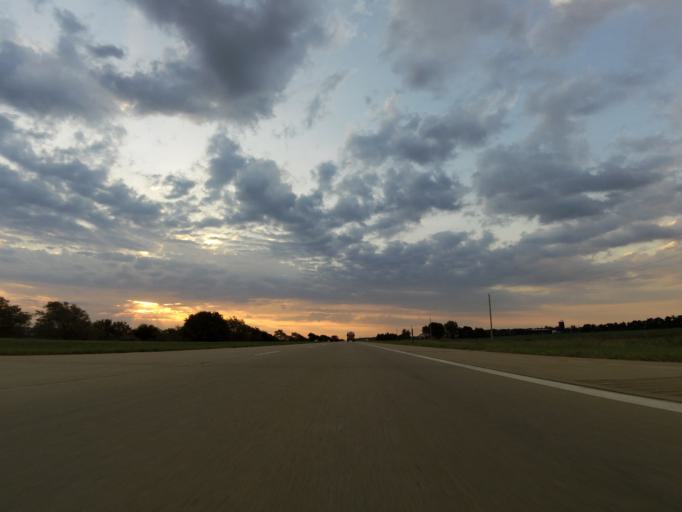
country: US
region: Kansas
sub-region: Reno County
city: Haven
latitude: 37.8905
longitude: -97.7533
